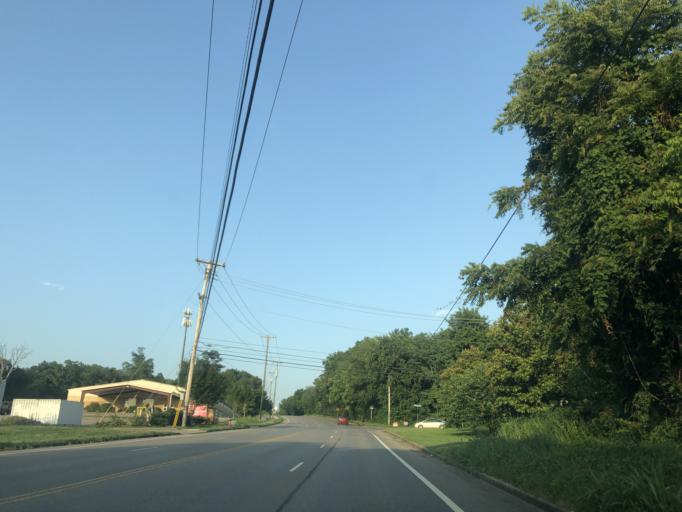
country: US
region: Tennessee
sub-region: Davidson County
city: Lakewood
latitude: 36.1419
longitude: -86.6382
